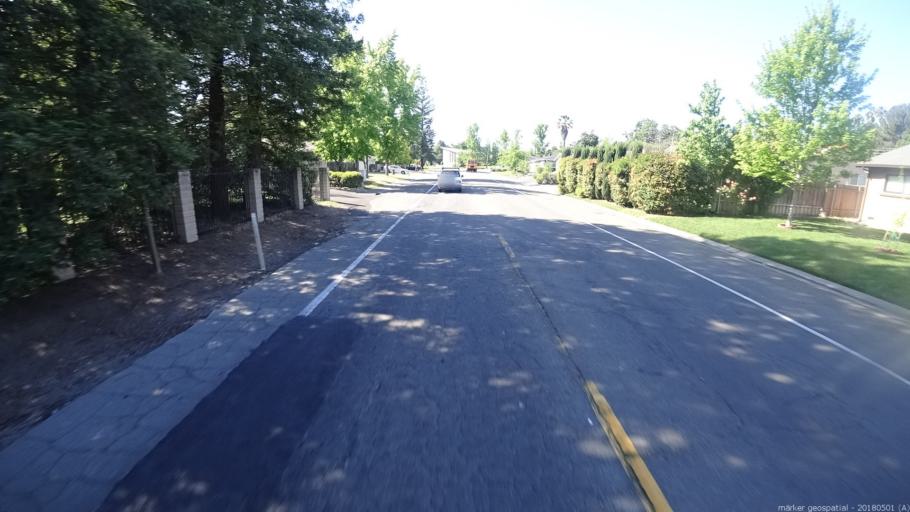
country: US
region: California
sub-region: Sacramento County
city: Arden-Arcade
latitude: 38.6392
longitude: -121.3690
